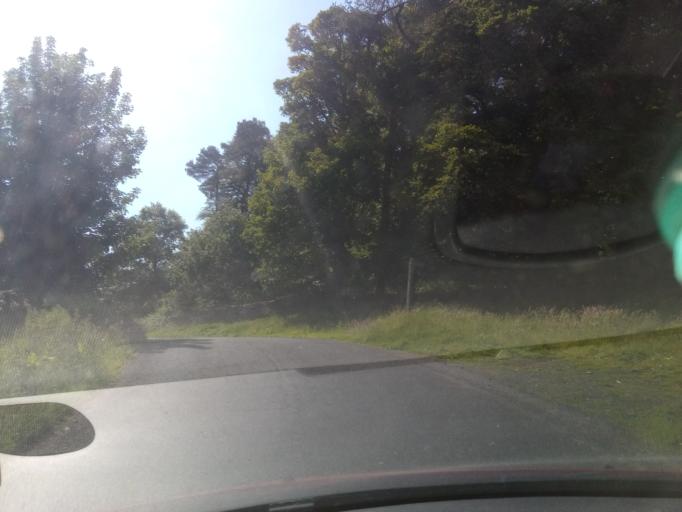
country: GB
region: Scotland
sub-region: The Scottish Borders
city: Peebles
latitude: 55.4981
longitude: -3.2177
